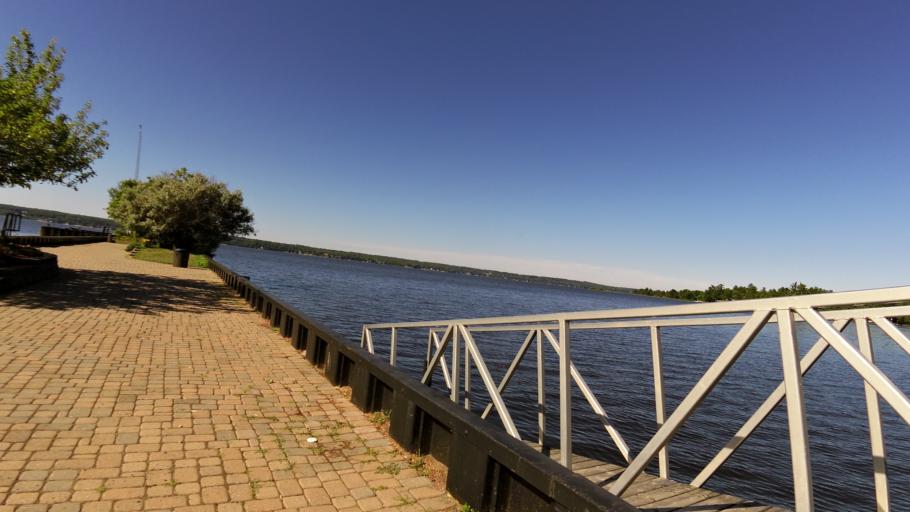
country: CA
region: Quebec
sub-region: Outaouais
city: Shawville
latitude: 45.5169
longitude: -76.4295
